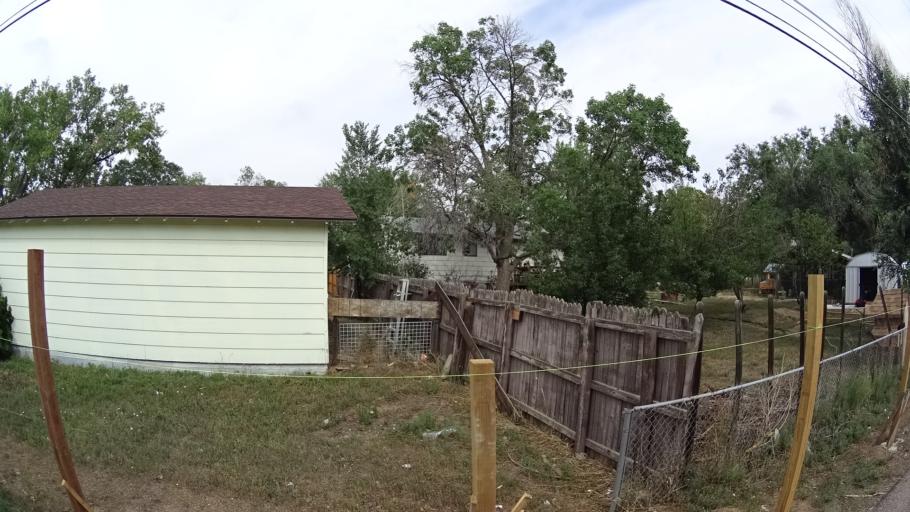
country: US
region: Colorado
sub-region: El Paso County
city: Colorado Springs
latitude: 38.8843
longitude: -104.7948
